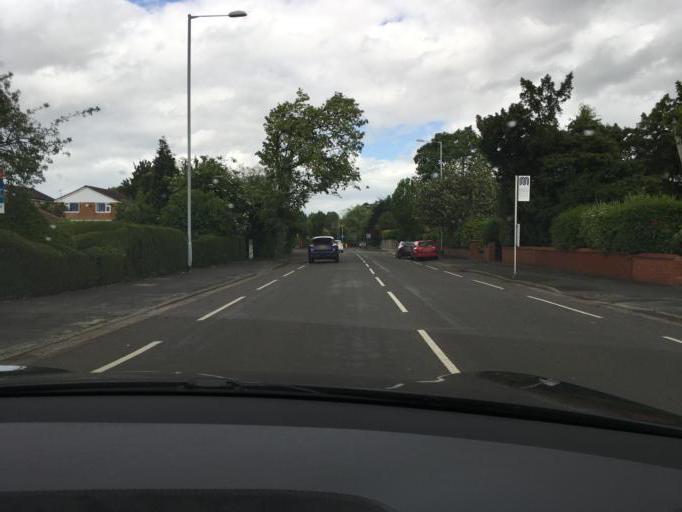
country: GB
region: England
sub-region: Borough of Stockport
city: Hazel Grove
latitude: 53.3729
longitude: -2.1235
